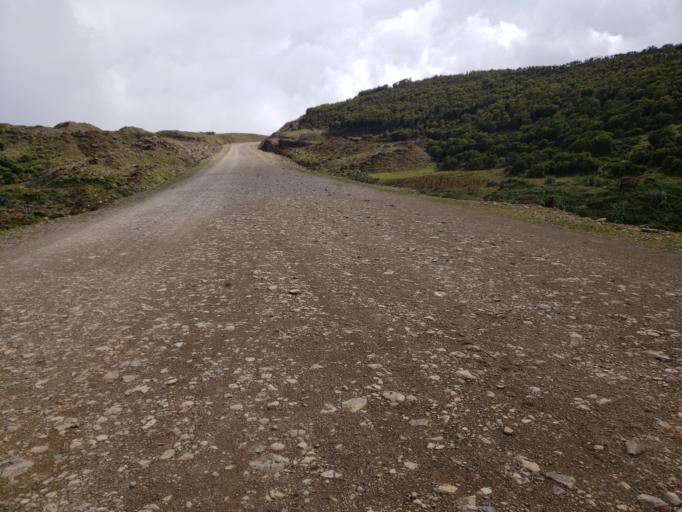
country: ET
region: Oromiya
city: Dodola
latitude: 6.7534
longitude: 39.4285
